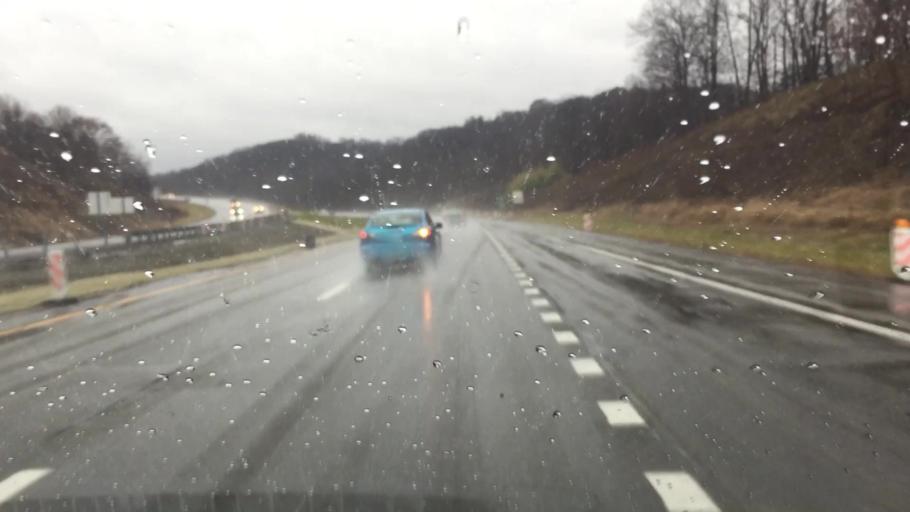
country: US
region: Pennsylvania
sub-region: Allegheny County
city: Ben Avon
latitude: 40.5306
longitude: -80.0721
